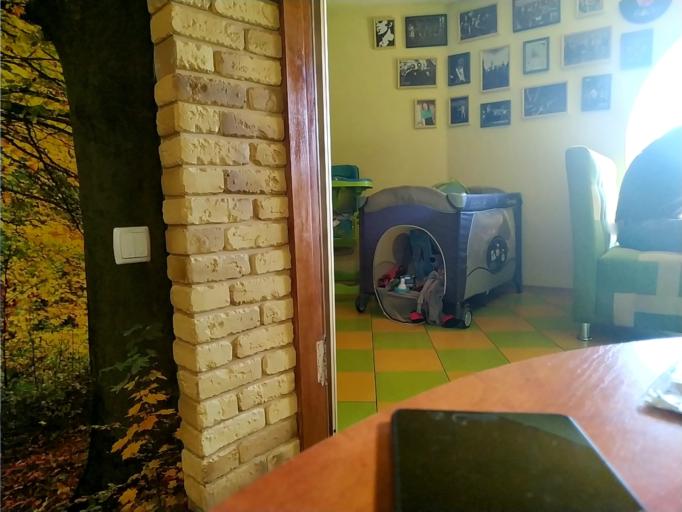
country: RU
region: Rjazan
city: Putyatino
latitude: 54.0775
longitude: 41.1662
